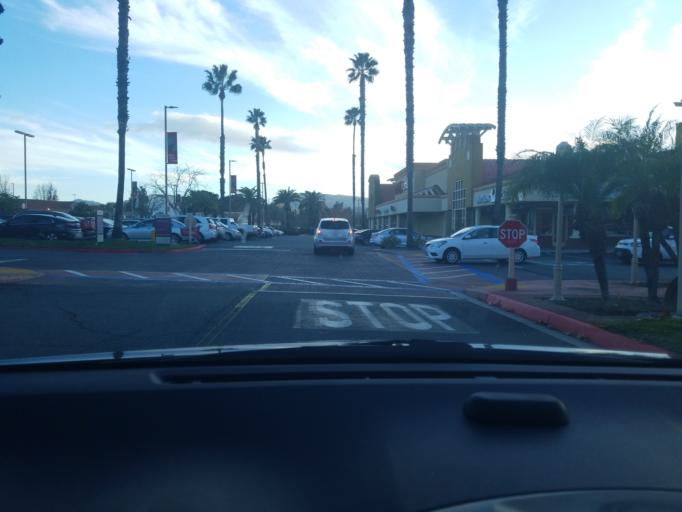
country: US
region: California
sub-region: Riverside County
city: Temecula
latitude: 33.5064
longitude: -117.1469
